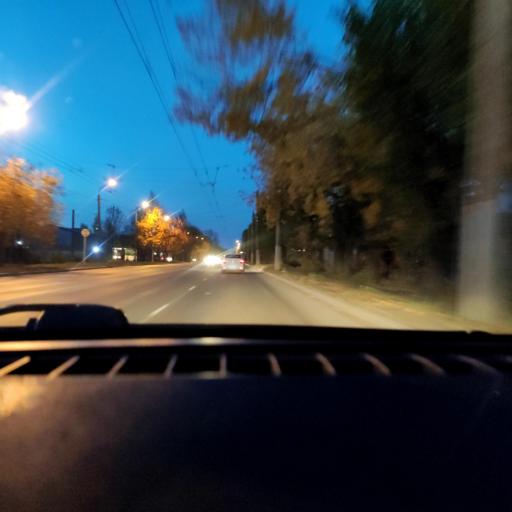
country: RU
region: Perm
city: Perm
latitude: 57.9713
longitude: 56.2459
